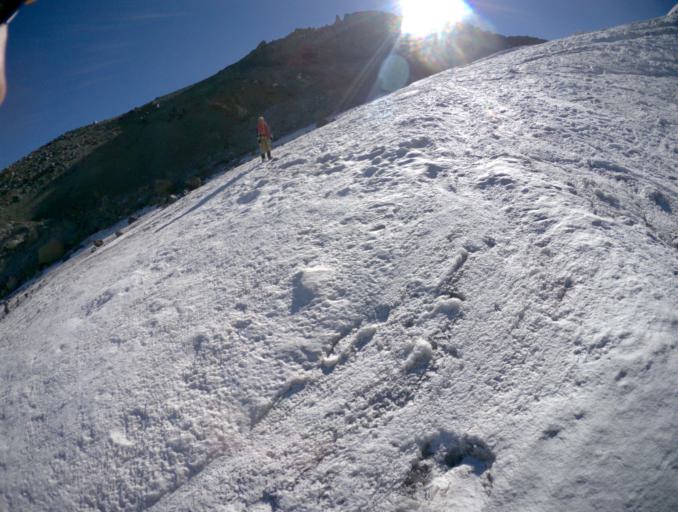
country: RU
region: Kabardino-Balkariya
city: Terskol
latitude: 43.3877
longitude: 42.4342
